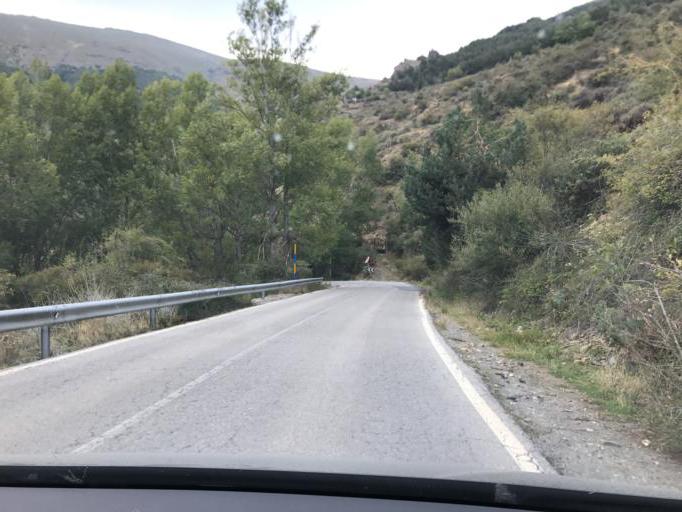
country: ES
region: Andalusia
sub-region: Provincia de Almeria
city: Bayarcal
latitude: 37.0906
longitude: -3.0281
